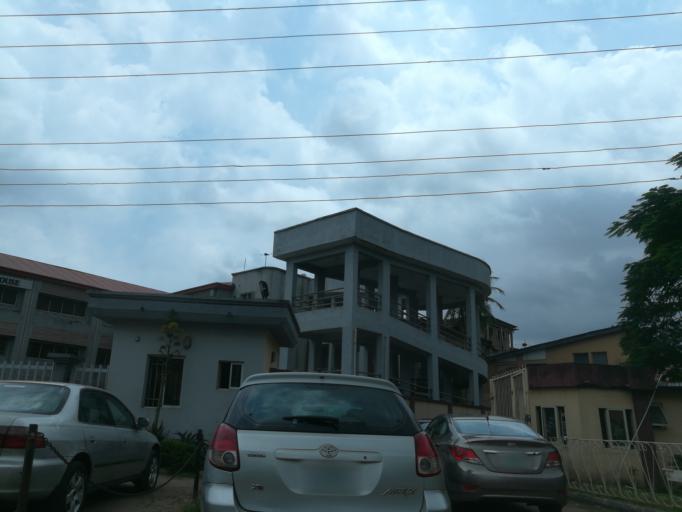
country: NG
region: Lagos
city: Ikeja
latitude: 6.5878
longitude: 3.3461
